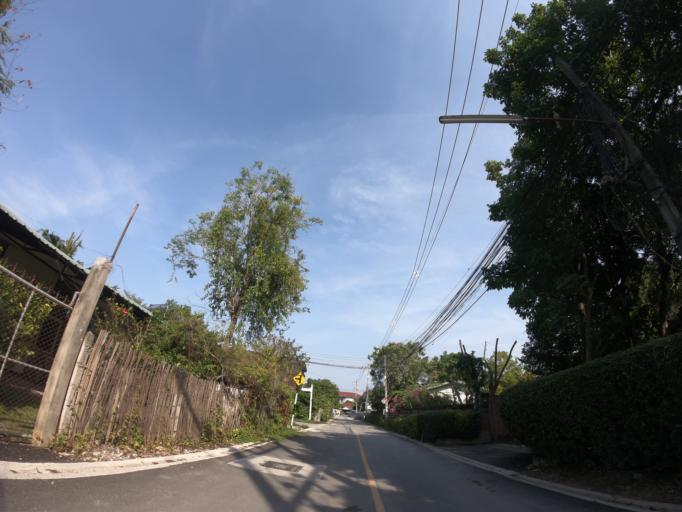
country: TH
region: Chiang Mai
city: Chiang Mai
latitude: 18.8165
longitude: 98.9849
